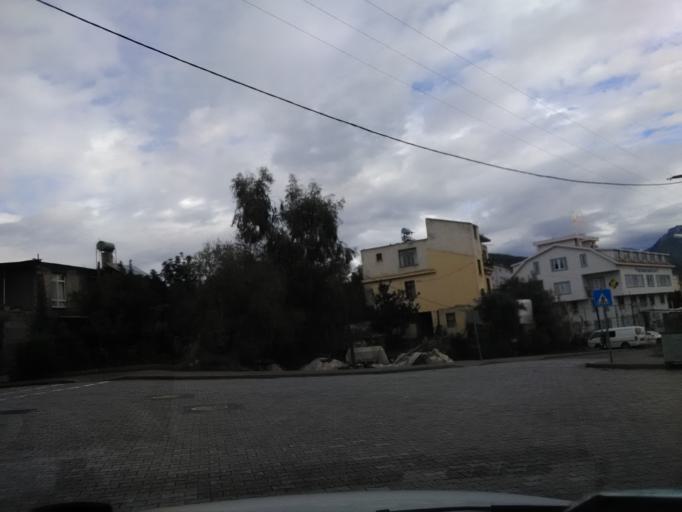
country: TR
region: Antalya
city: Gazipasa
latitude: 36.2713
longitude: 32.3145
